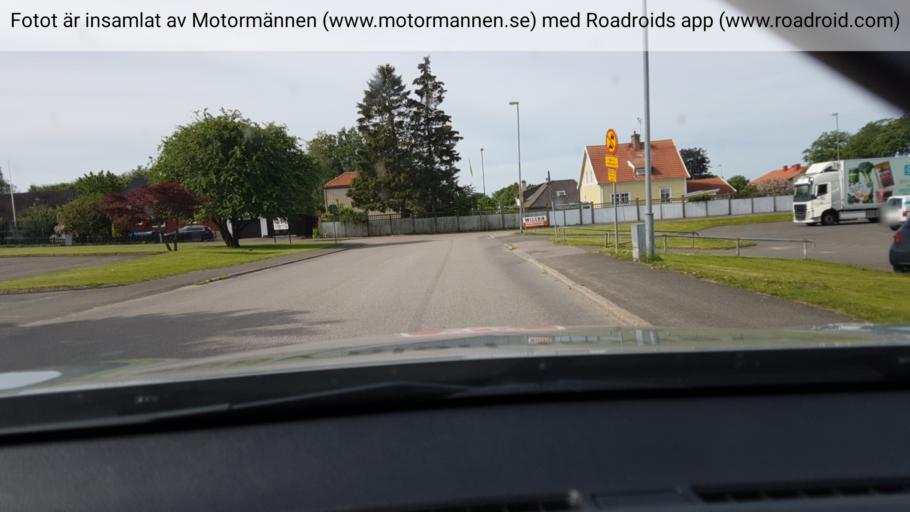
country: SE
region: Vaestra Goetaland
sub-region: Falkopings Kommun
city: Falkoeping
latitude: 58.1631
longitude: 13.5621
